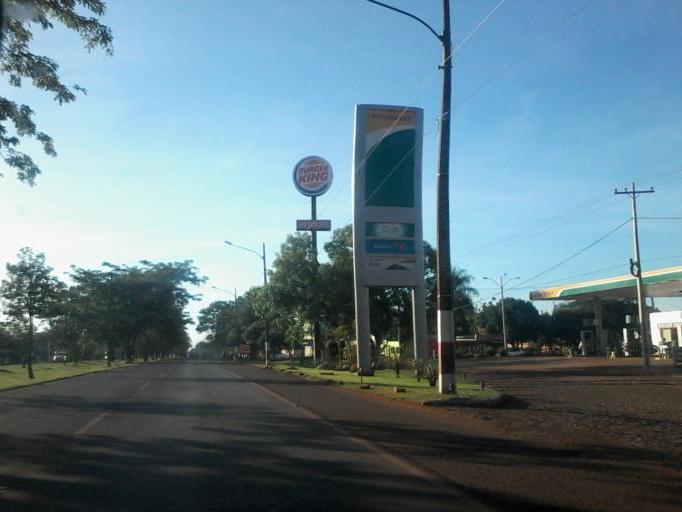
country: PY
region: Alto Parana
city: Ciudad del Este
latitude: -25.4357
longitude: -54.6367
